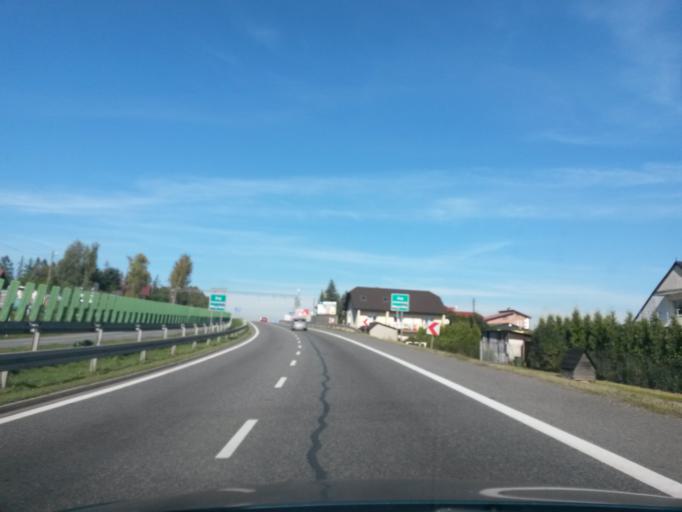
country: PL
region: Lesser Poland Voivodeship
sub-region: Powiat krakowski
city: Mogilany
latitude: 49.9539
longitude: 19.8901
